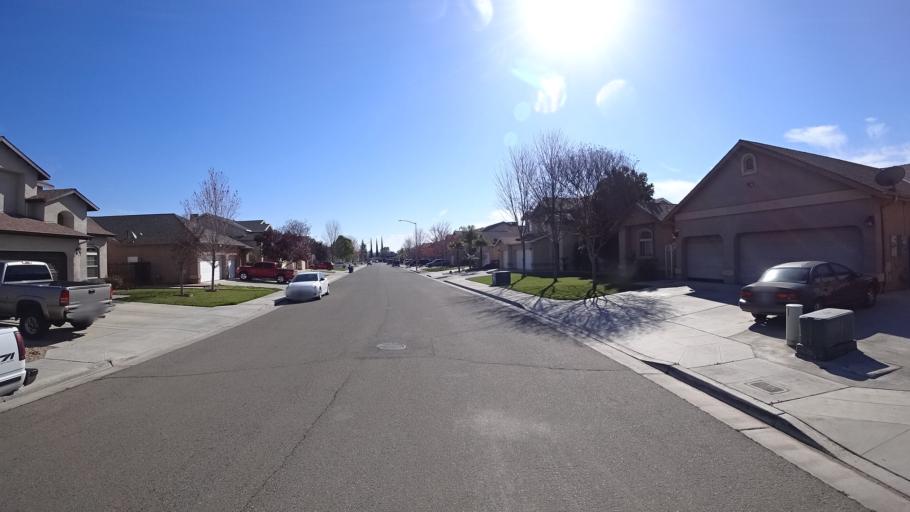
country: US
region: California
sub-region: Fresno County
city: West Park
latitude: 36.7994
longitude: -119.8878
